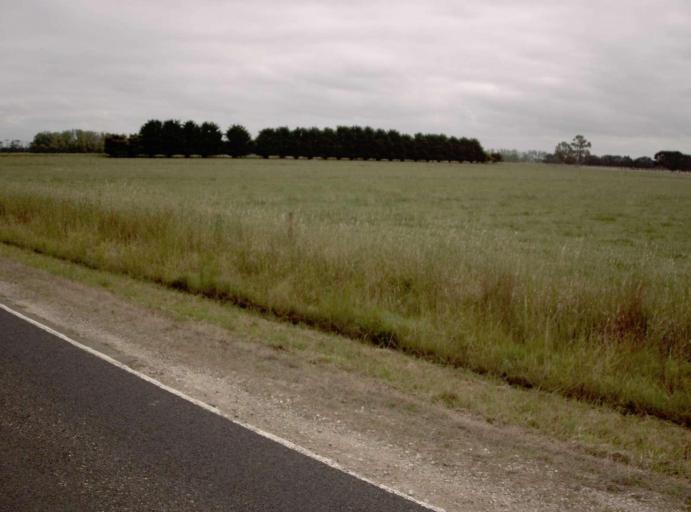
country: AU
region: Victoria
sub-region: Wellington
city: Sale
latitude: -38.0505
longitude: 146.9540
